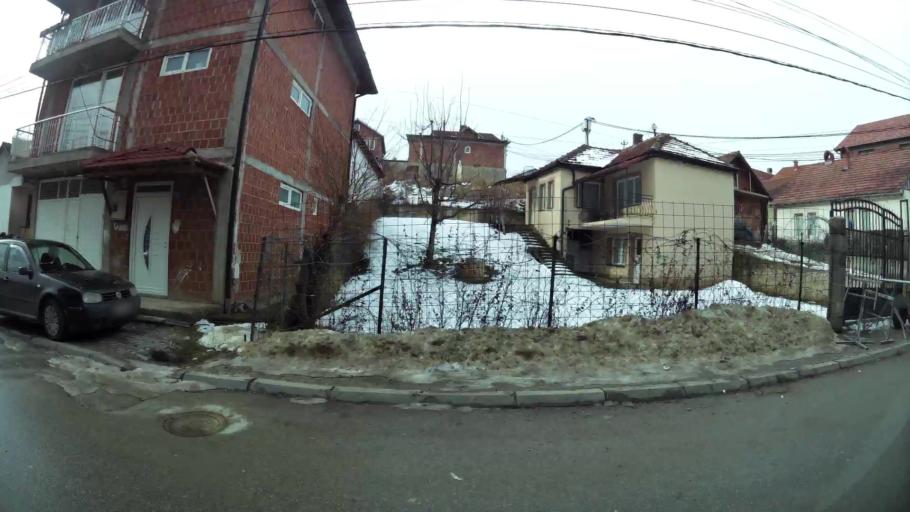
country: XK
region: Pristina
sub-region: Komuna e Prishtines
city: Pristina
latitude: 42.6816
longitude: 21.1631
